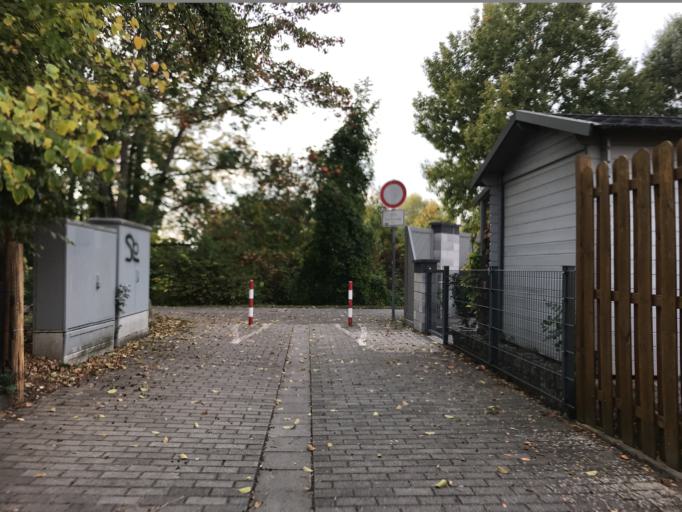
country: DE
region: Rheinland-Pfalz
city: Ingelheim am Rhein
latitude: 49.9716
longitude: 8.0516
